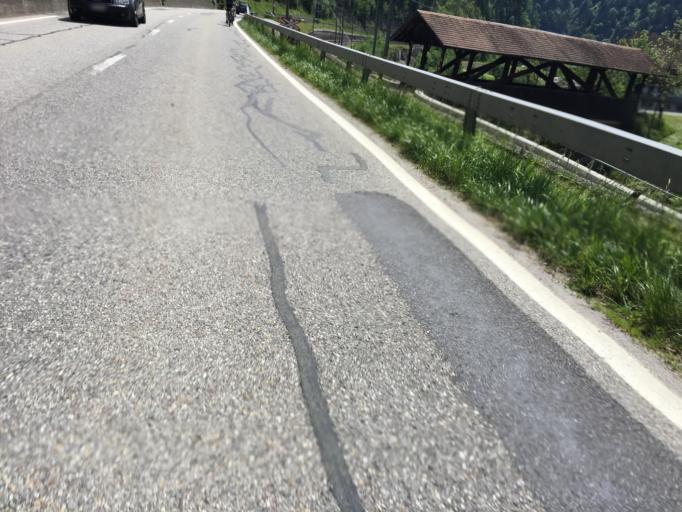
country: CH
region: Bern
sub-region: Emmental District
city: Trubschachen
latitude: 46.9198
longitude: 7.8531
